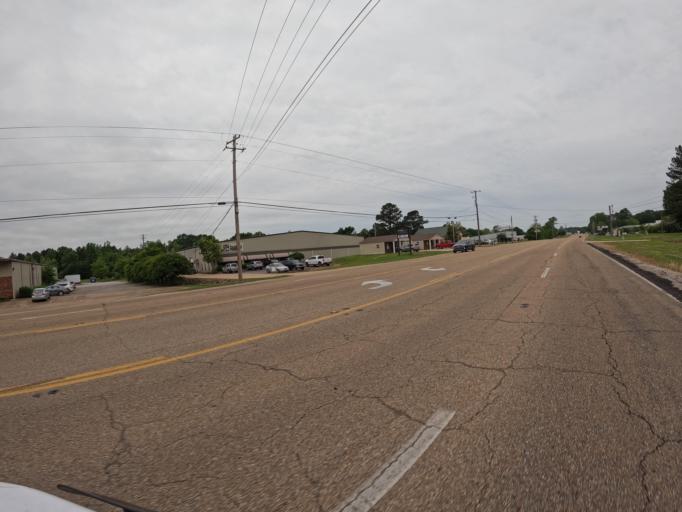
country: US
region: Mississippi
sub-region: Lee County
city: Tupelo
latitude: 34.2859
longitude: -88.7395
